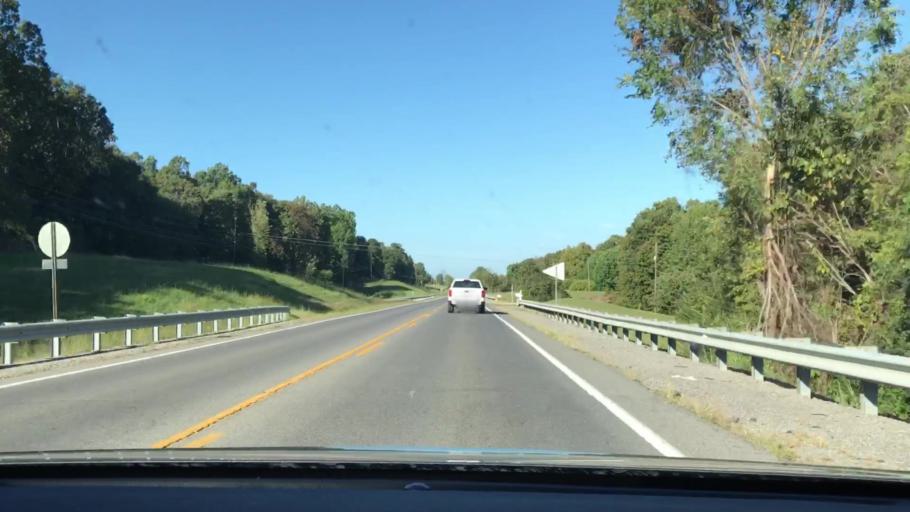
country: US
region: Kentucky
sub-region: Marshall County
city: Calvert City
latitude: 37.0046
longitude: -88.3750
